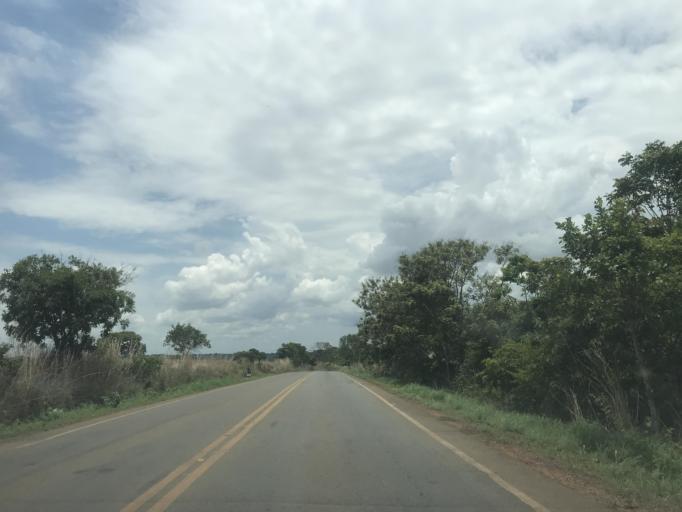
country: BR
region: Goias
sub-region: Vianopolis
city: Vianopolis
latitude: -16.7389
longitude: -48.4477
